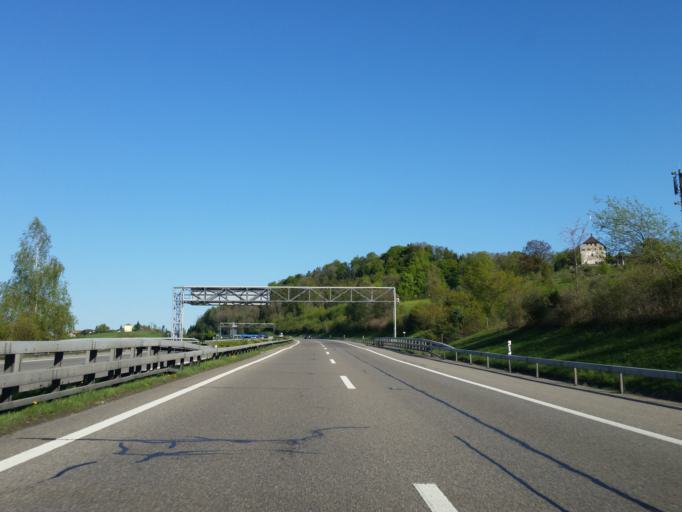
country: CH
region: Appenzell Ausserrhoden
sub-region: Bezirk Hinterland
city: Herisau
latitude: 47.4105
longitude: 9.2891
